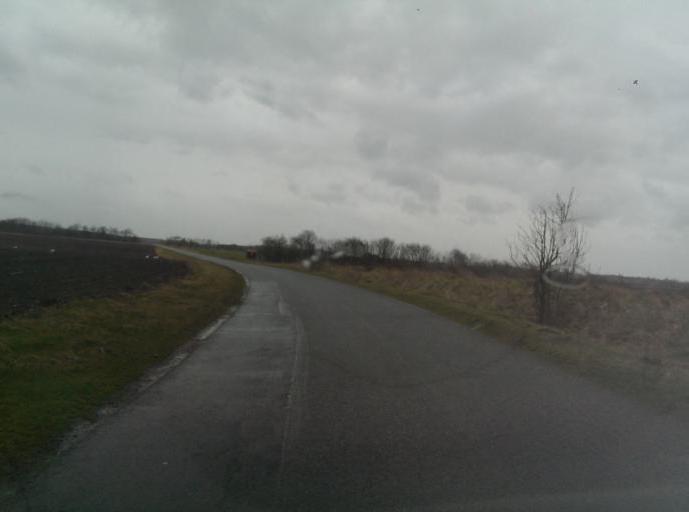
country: DK
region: Central Jutland
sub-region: Ringkobing-Skjern Kommune
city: Skjern
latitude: 56.0105
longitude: 8.4043
